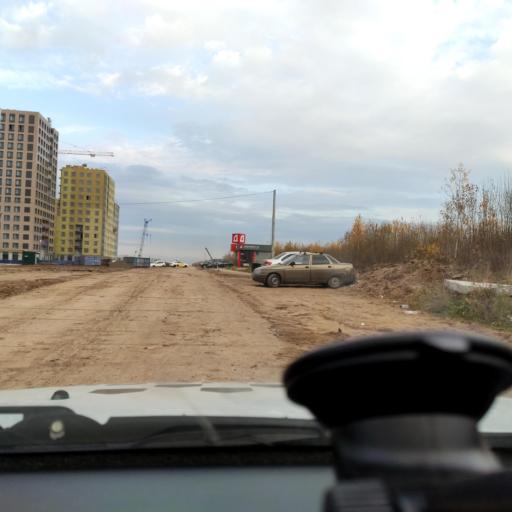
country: RU
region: Perm
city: Perm
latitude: 58.0099
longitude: 56.3333
